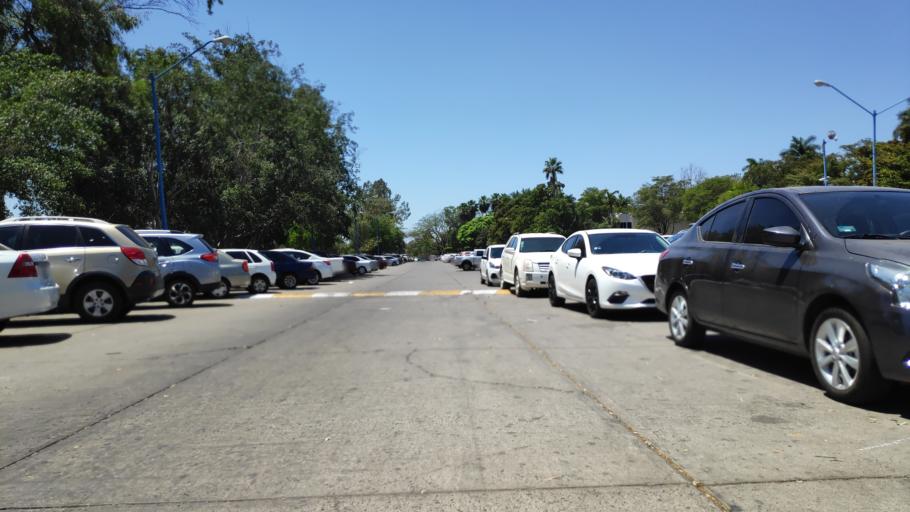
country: MX
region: Sinaloa
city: Culiacan
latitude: 24.8256
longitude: -107.3808
